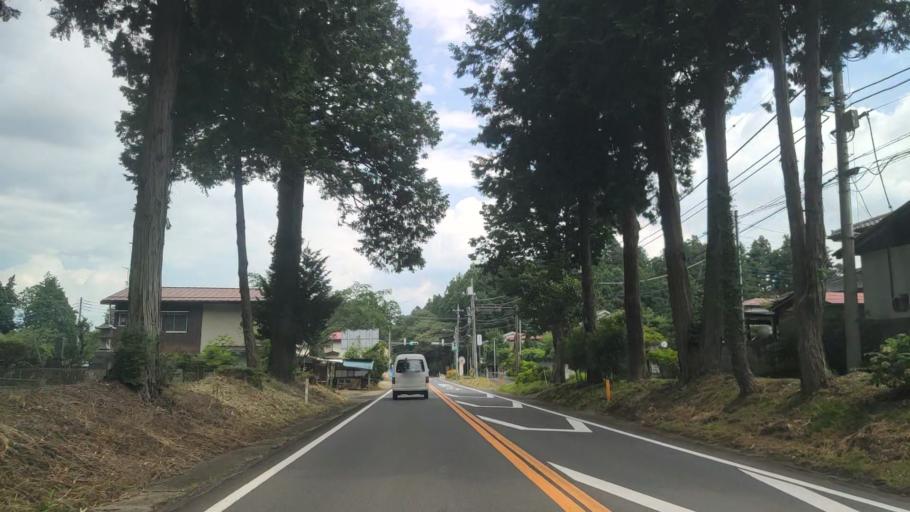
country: JP
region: Tochigi
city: Imaichi
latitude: 36.6813
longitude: 139.7919
